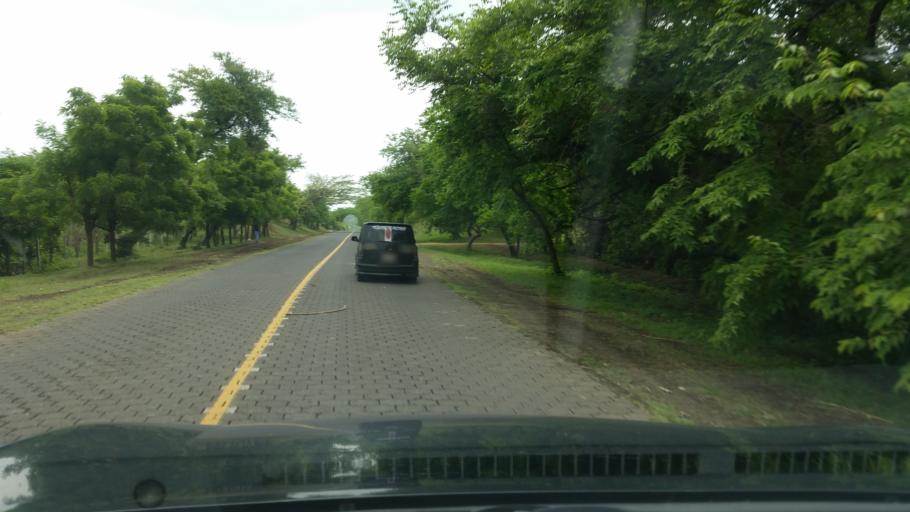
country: NI
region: Managua
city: Masachapa
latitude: 11.8494
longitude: -86.5171
